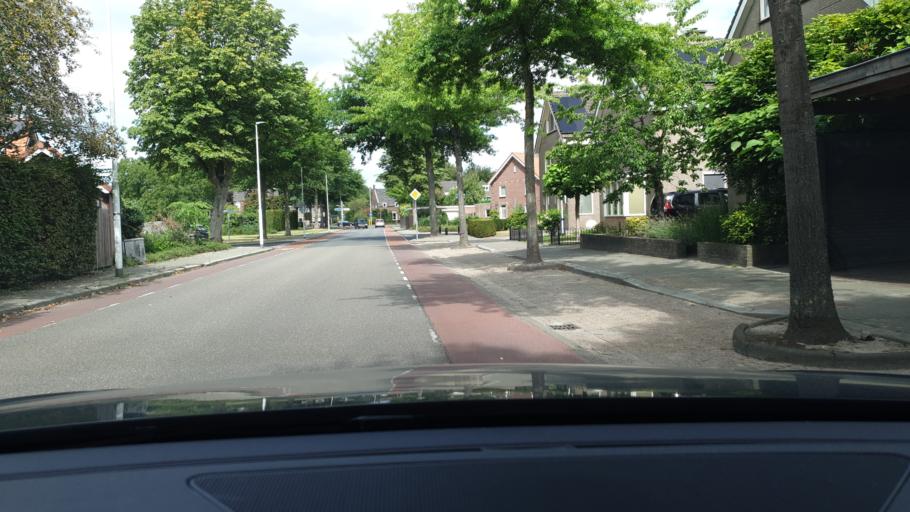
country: NL
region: North Brabant
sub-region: Gemeente Best
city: Best
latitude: 51.5085
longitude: 5.3850
